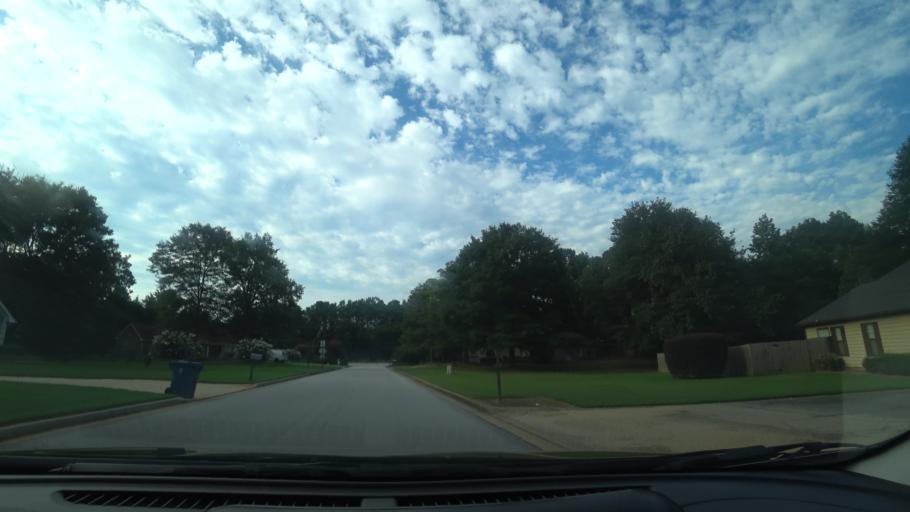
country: US
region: Georgia
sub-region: Newton County
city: Porterdale
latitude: 33.6133
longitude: -83.9488
